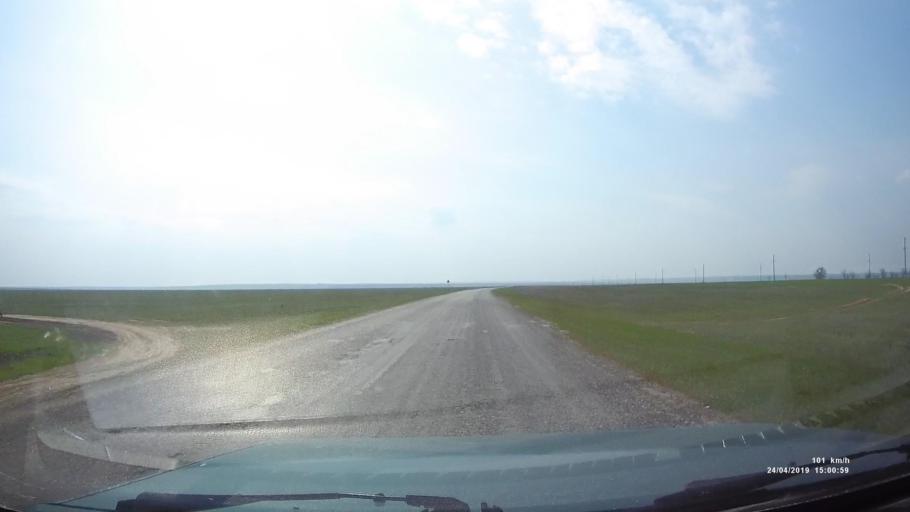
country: RU
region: Rostov
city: Remontnoye
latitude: 46.5654
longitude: 43.5435
